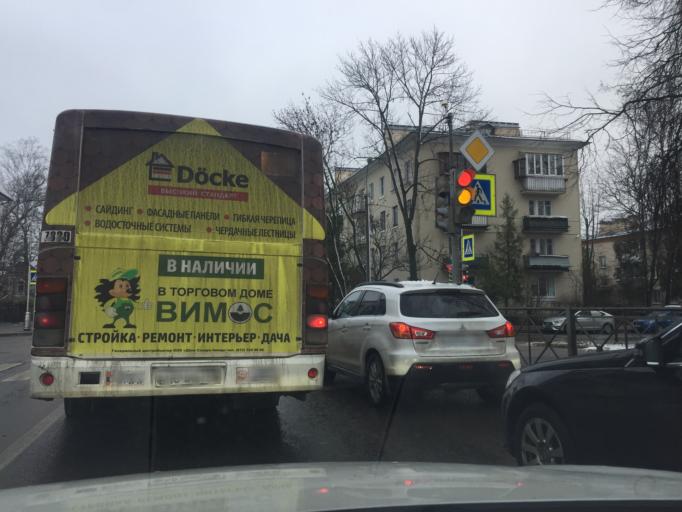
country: RU
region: St.-Petersburg
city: Pushkin
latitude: 59.7154
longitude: 30.4079
